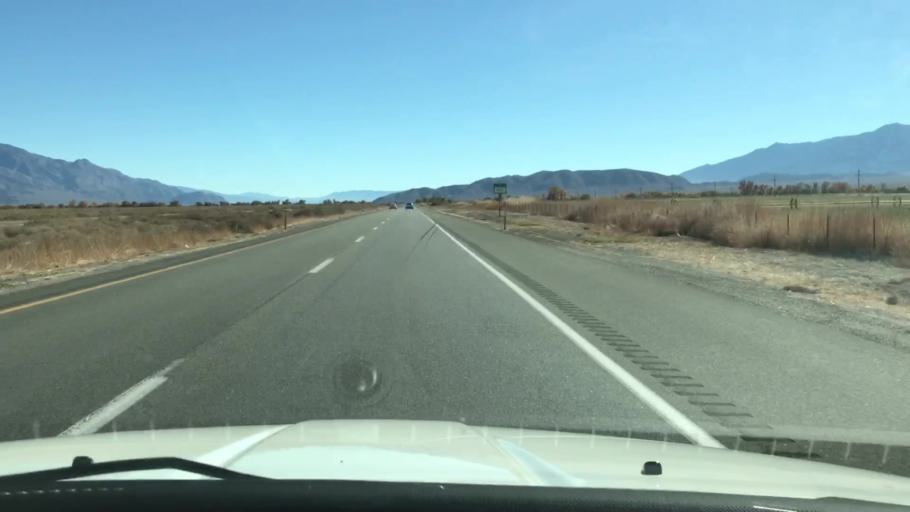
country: US
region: California
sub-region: Inyo County
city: Lone Pine
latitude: 36.7550
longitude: -118.1657
